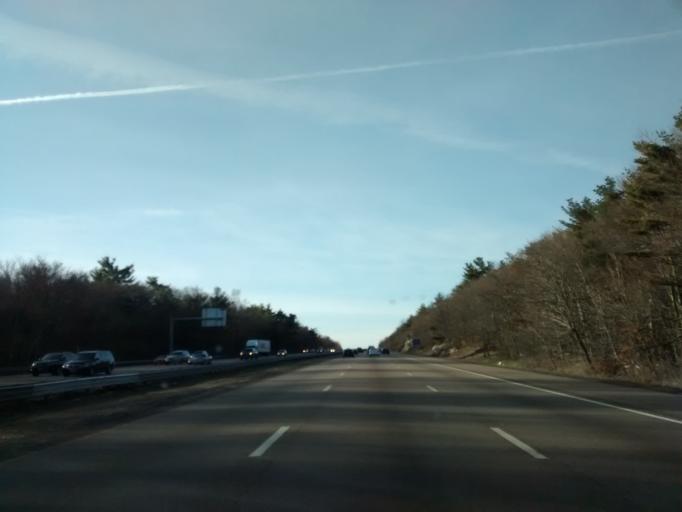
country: US
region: Massachusetts
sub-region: Norfolk County
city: Randolph
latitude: 42.1675
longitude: -71.0718
